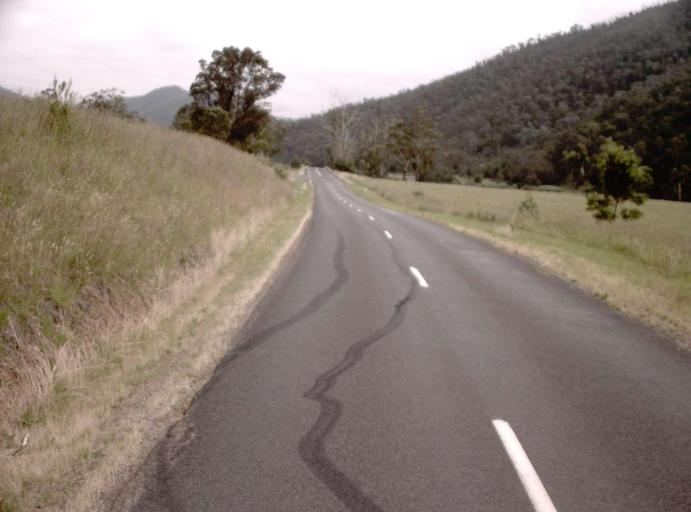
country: AU
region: Victoria
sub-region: Wellington
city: Heyfield
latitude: -37.7659
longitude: 146.6682
